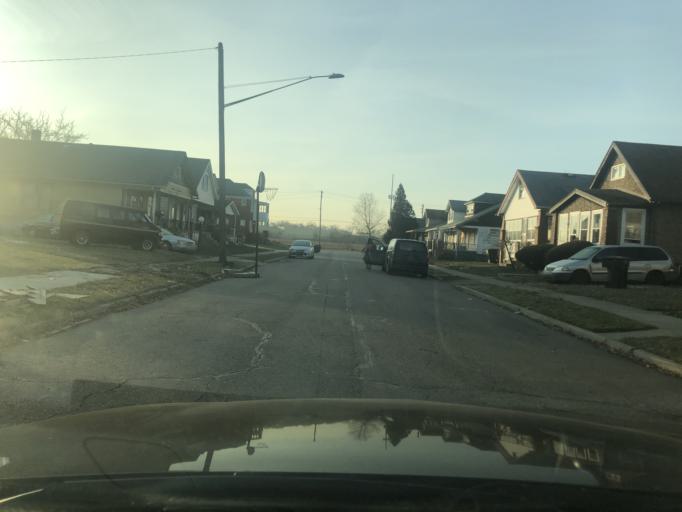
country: US
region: Michigan
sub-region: Wayne County
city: Highland Park
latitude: 42.3999
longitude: -83.1331
